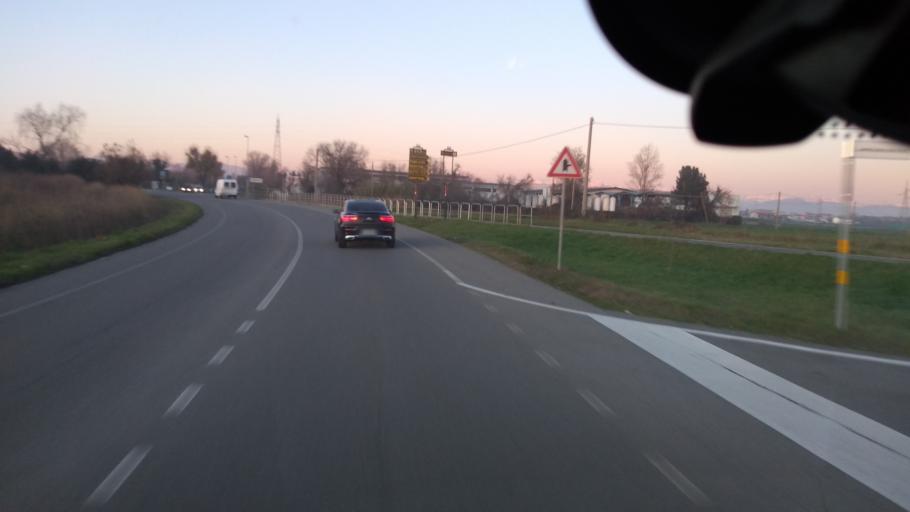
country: IT
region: Lombardy
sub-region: Provincia di Bergamo
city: Calvenzano
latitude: 45.5070
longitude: 9.5952
